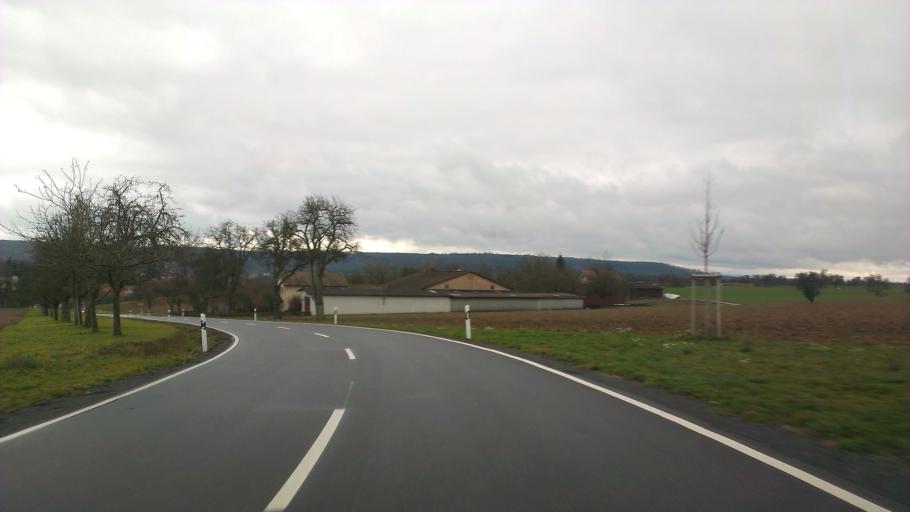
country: DE
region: Baden-Wuerttemberg
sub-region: Regierungsbezirk Stuttgart
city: Zaberfeld
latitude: 49.0820
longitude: 8.8951
